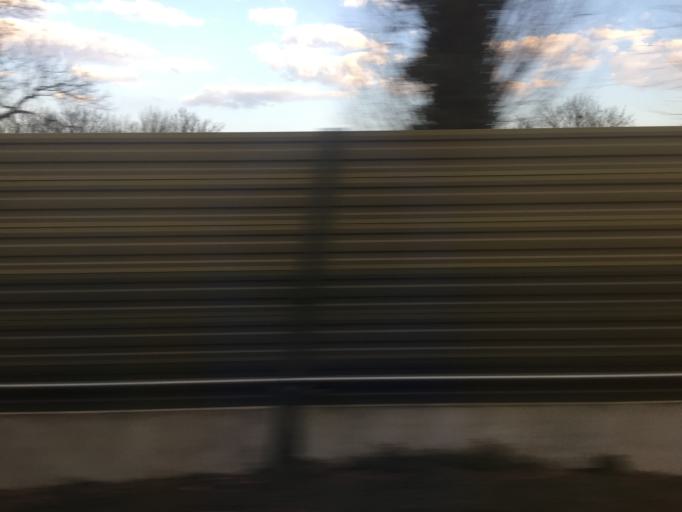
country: DE
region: Schleswig-Holstein
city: Elmshorn
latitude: 53.7425
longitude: 9.6631
